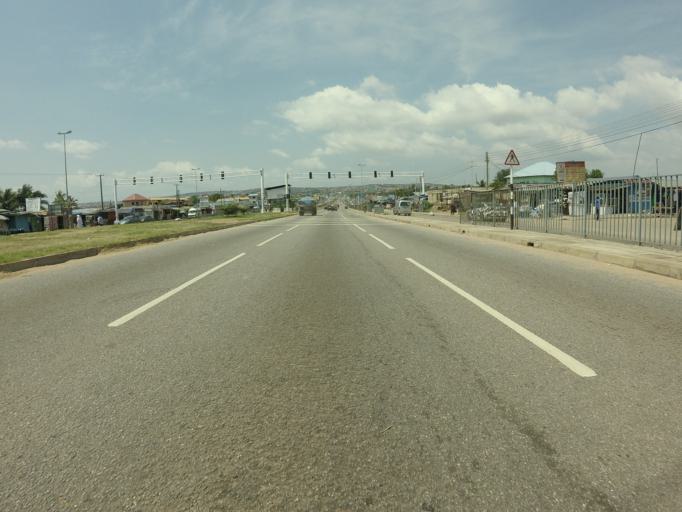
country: GH
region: Greater Accra
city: Gbawe
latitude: 5.5858
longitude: -0.2768
